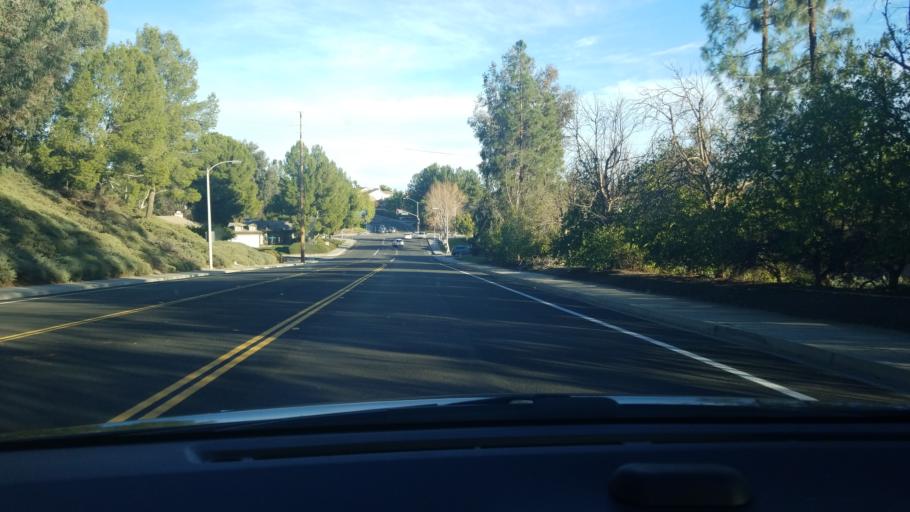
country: US
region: California
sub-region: Riverside County
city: Temecula
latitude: 33.5107
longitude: -117.1261
